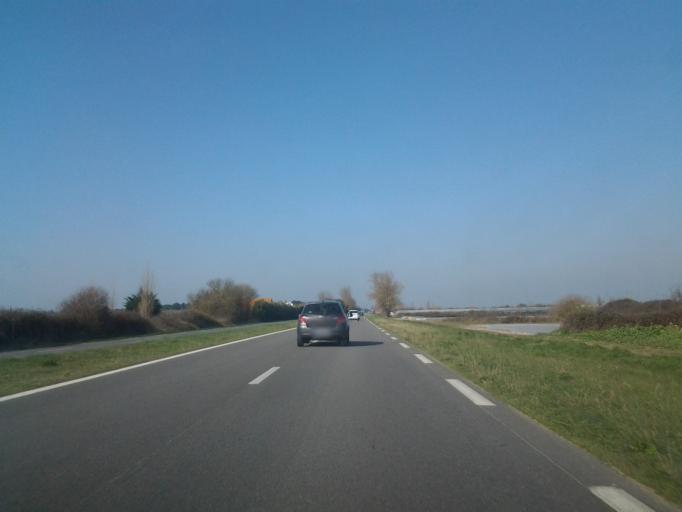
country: FR
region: Pays de la Loire
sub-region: Departement de la Vendee
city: Barbatre
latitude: 46.9584
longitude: -2.1966
